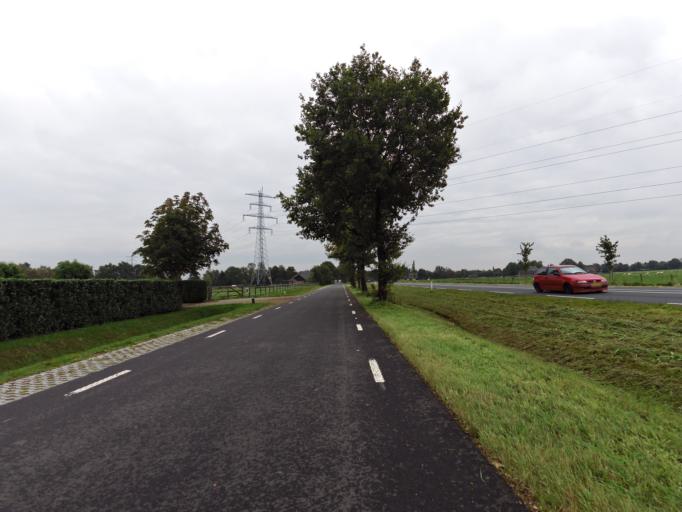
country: NL
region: Gelderland
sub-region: Oude IJsselstreek
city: Gendringen
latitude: 51.9093
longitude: 6.3476
